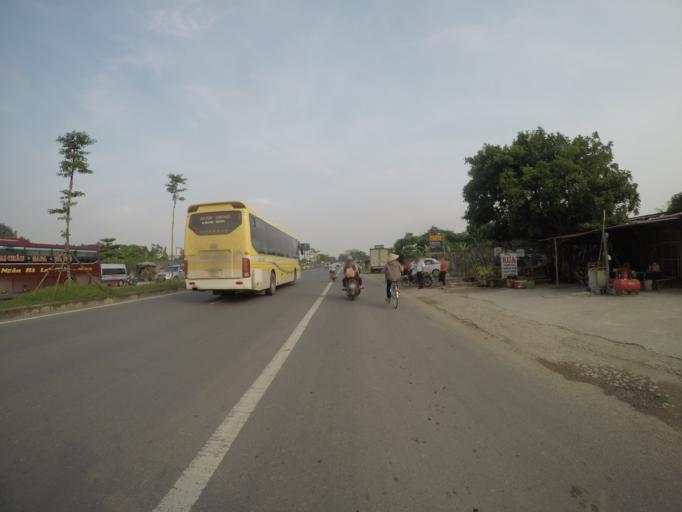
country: VN
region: Ha Noi
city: Me Linh
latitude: 21.2181
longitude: 105.7754
